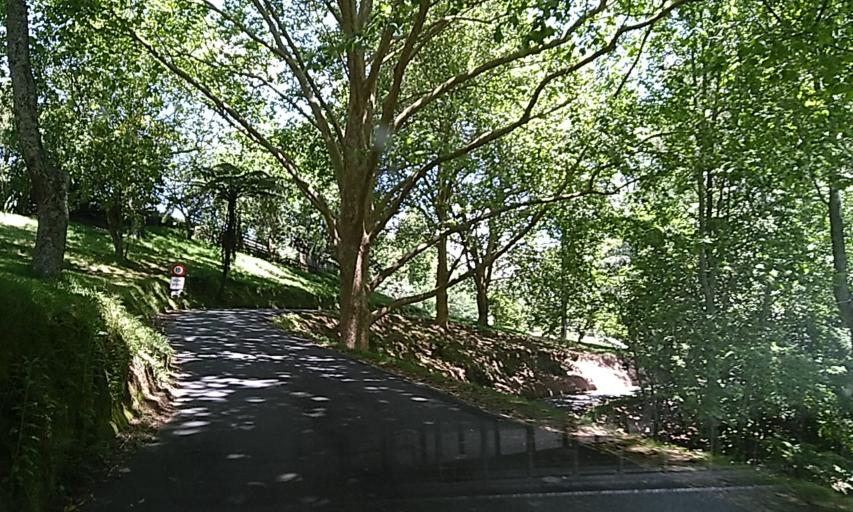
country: NZ
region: Bay of Plenty
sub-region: Tauranga City
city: Tauranga
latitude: -37.8078
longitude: 176.0462
